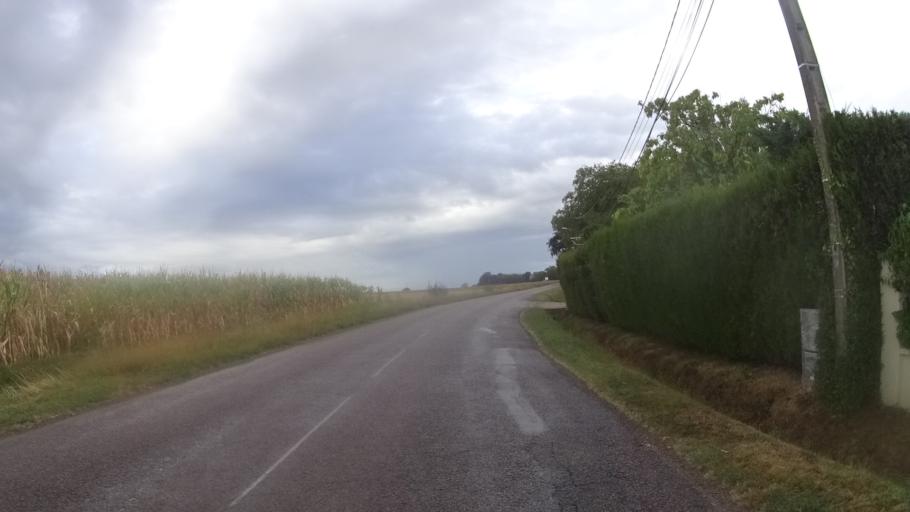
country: FR
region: Bourgogne
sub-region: Departement de Saone-et-Loire
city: Gergy
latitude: 46.9509
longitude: 4.9536
